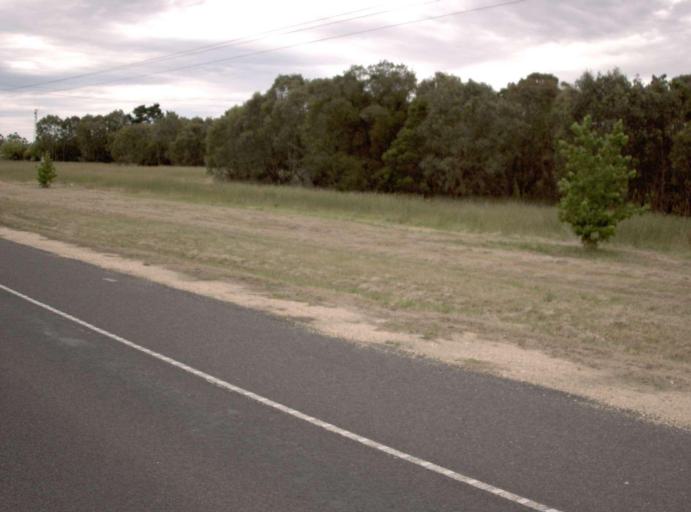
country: AU
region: Victoria
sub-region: Wellington
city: Sale
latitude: -38.1227
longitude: 147.0692
